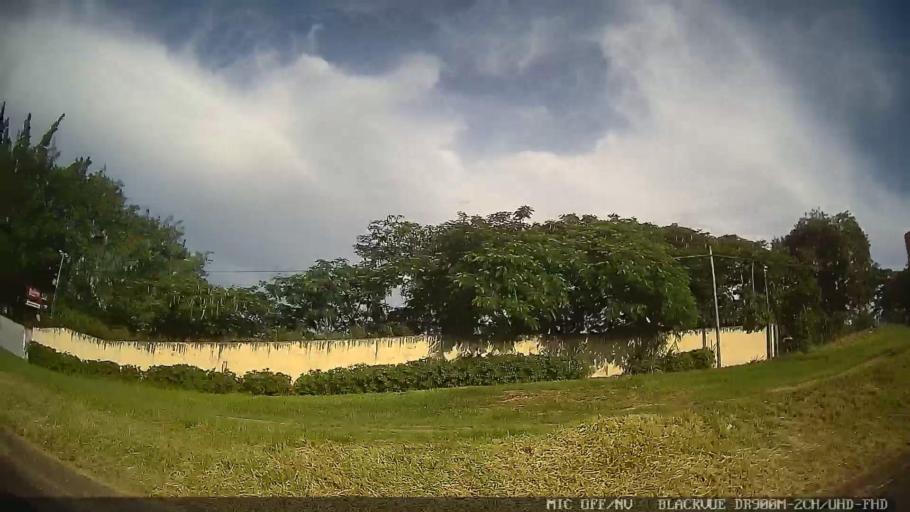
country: BR
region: Sao Paulo
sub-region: Tiete
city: Tiete
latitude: -23.1128
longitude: -47.6972
